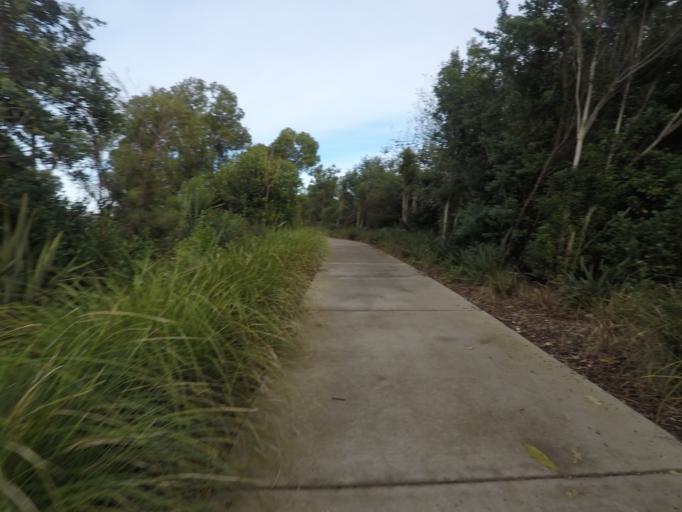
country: NZ
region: Auckland
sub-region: Auckland
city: Mangere
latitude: -36.9454
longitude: 174.8083
